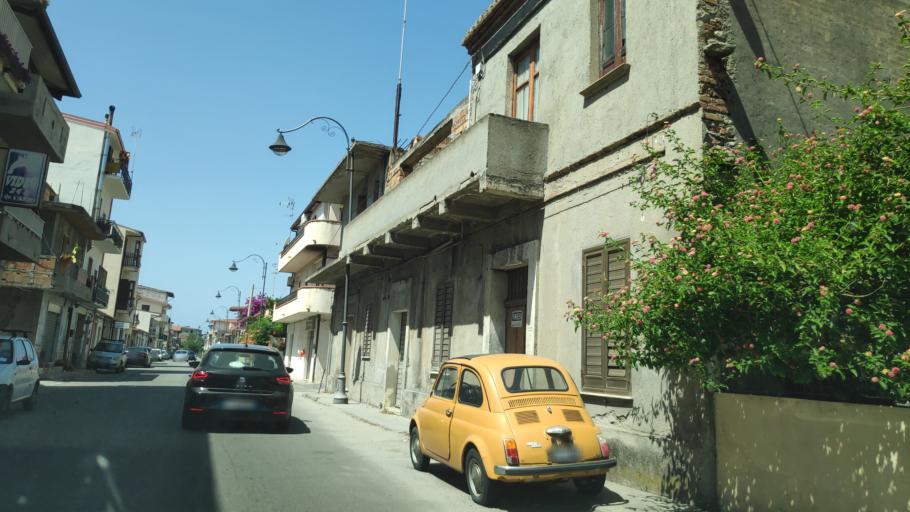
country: IT
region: Calabria
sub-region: Provincia di Reggio Calabria
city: Bova Marina
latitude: 37.9300
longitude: 15.9141
